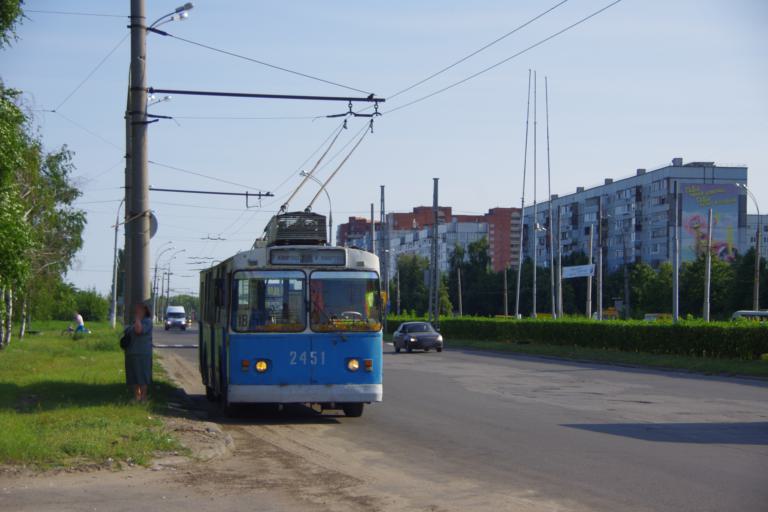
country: RU
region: Samara
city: Tol'yatti
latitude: 53.5064
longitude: 49.2922
